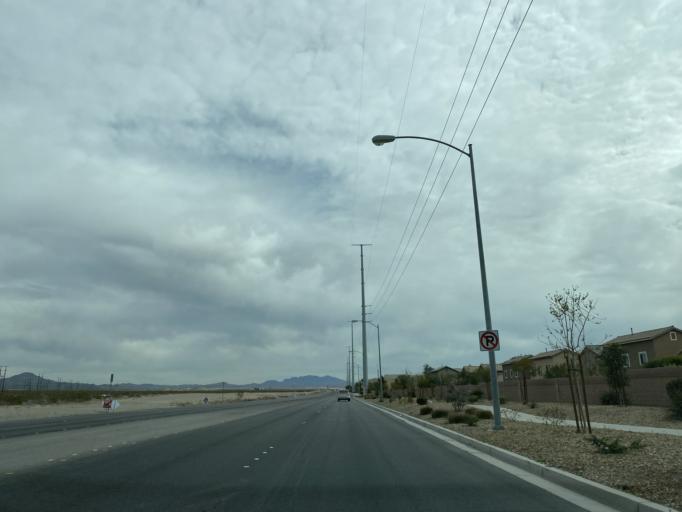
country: US
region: Nevada
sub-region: Clark County
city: Nellis Air Force Base
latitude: 36.2765
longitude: -115.0920
